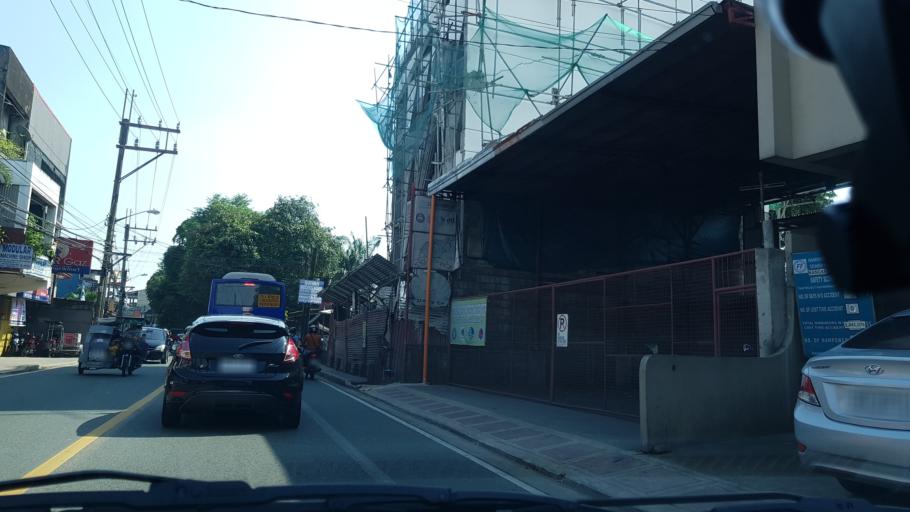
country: PH
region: Metro Manila
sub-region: Marikina
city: Calumpang
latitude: 14.6390
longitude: 121.0942
